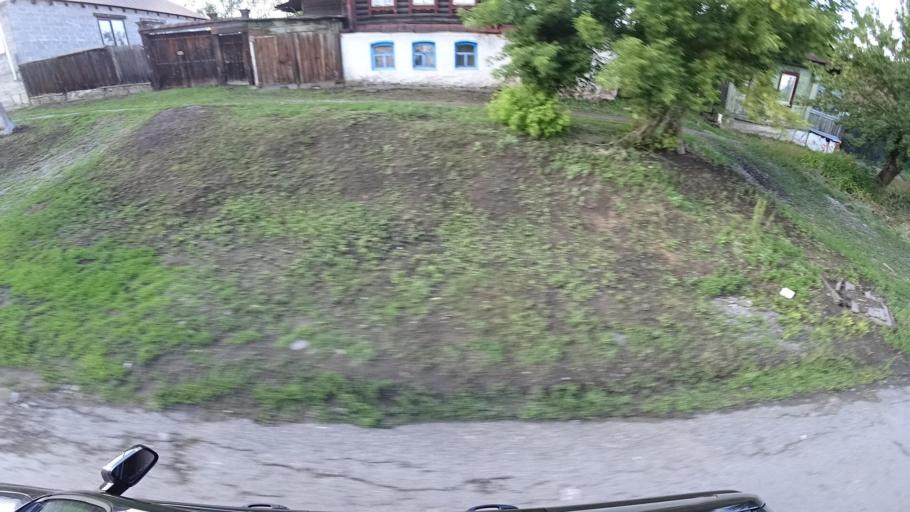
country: RU
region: Sverdlovsk
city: Kamyshlov
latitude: 56.8489
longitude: 62.7039
